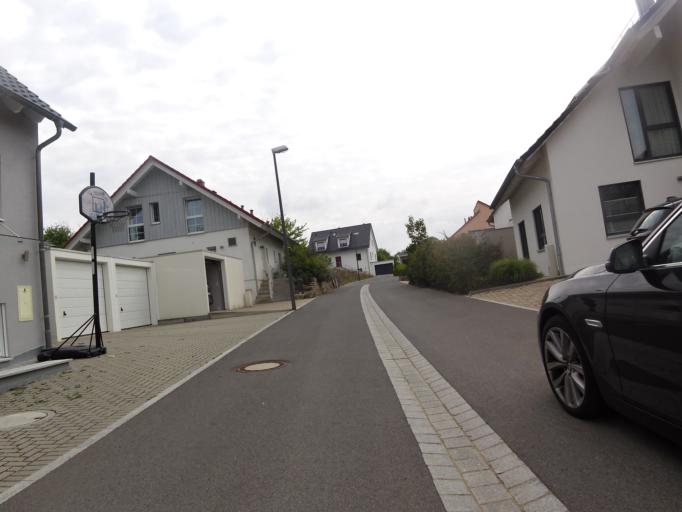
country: DE
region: Bavaria
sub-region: Regierungsbezirk Unterfranken
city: Hochberg
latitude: 49.7788
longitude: 9.8822
